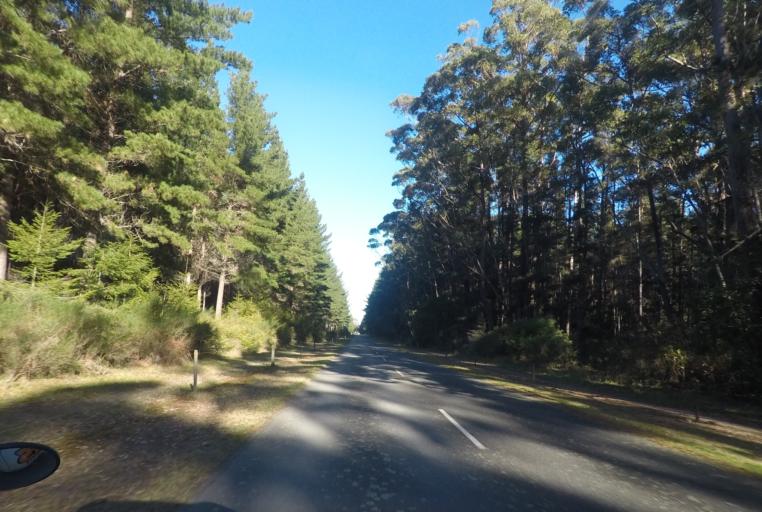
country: NZ
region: Tasman
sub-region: Tasman District
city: Mapua
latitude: -41.2689
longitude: 173.1510
